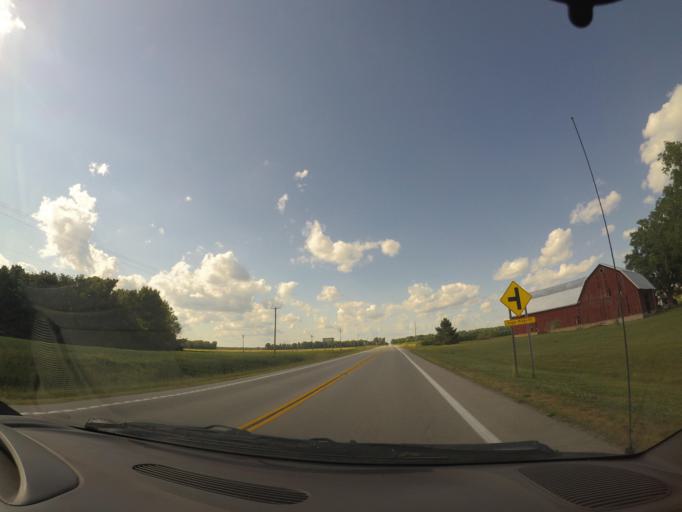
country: US
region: Ohio
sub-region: Wood County
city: Pemberville
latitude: 41.4267
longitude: -83.4154
